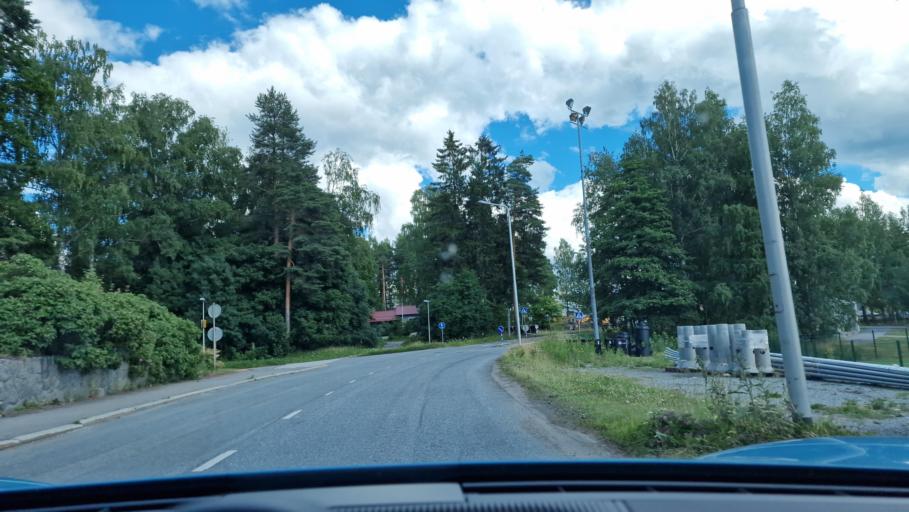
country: FI
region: Pirkanmaa
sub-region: Etelae-Pirkanmaa
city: Valkeakoski
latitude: 61.2719
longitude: 24.0260
